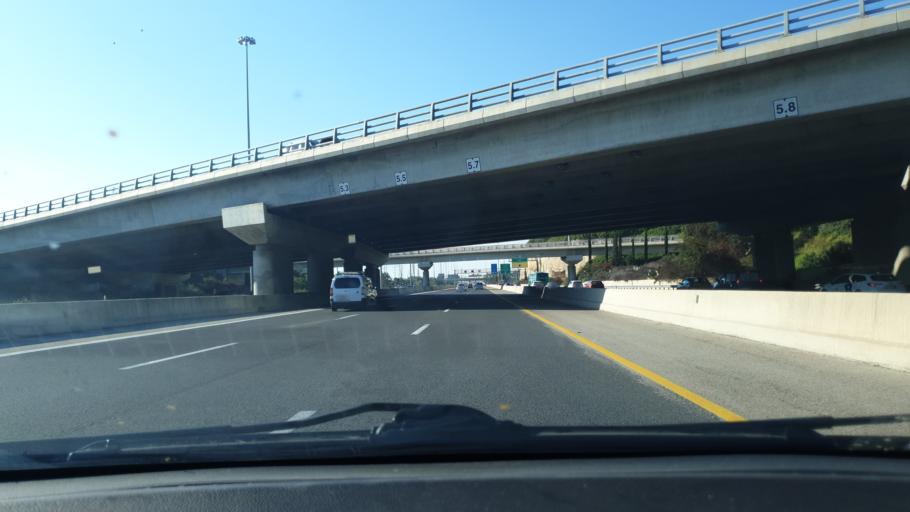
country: IL
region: Central District
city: Rishon LeZiyyon
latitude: 31.9580
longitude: 34.7756
